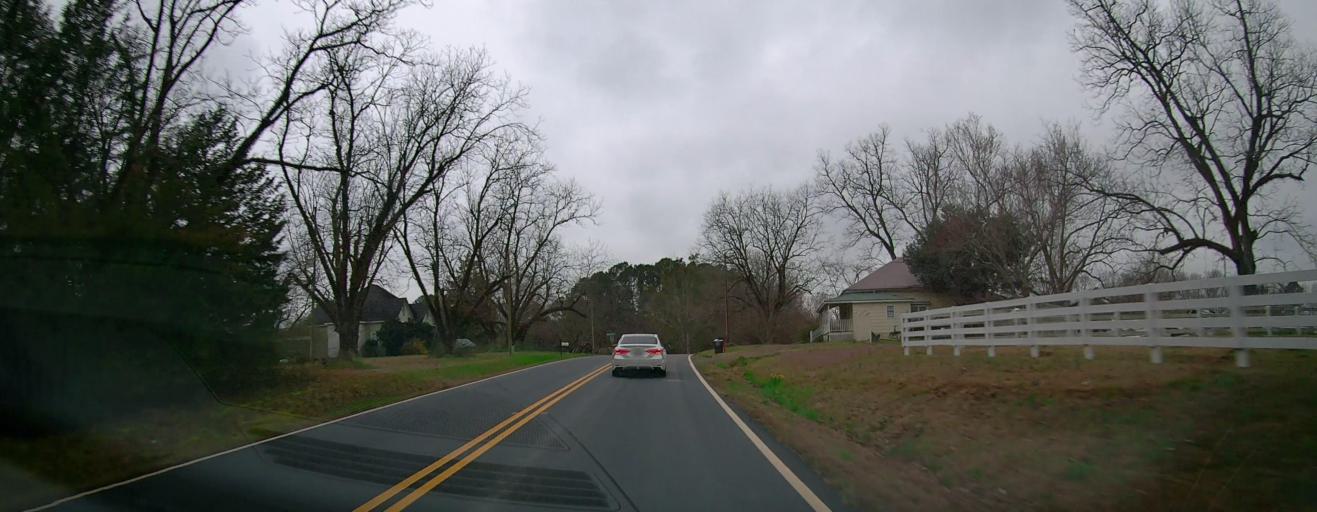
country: US
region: Georgia
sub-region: Pike County
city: Zebulon
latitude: 33.0578
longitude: -84.2644
